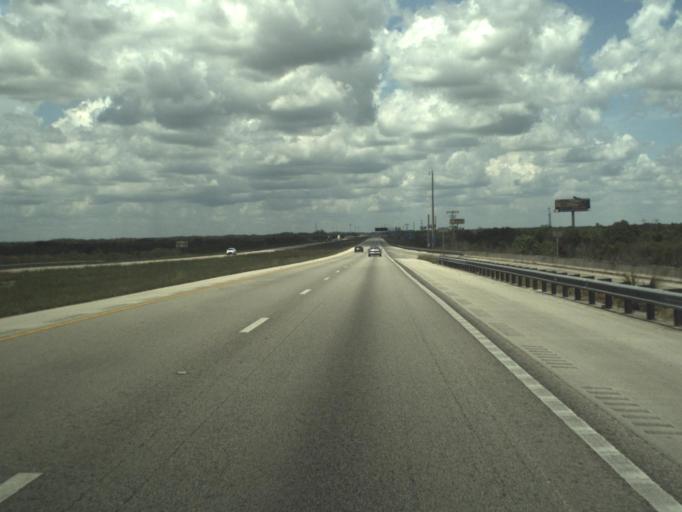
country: US
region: Florida
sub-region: Broward County
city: Weston
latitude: 26.1669
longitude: -80.8302
